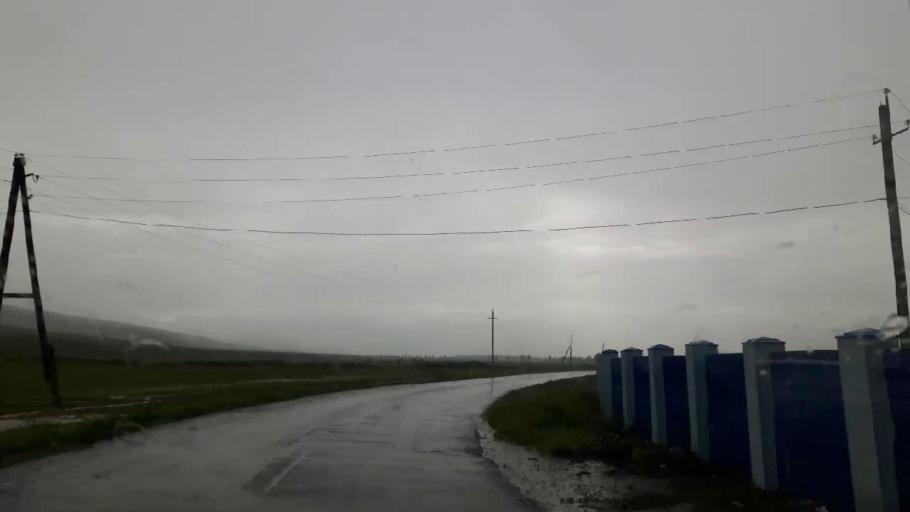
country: GE
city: Agara
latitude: 42.0149
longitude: 43.8175
